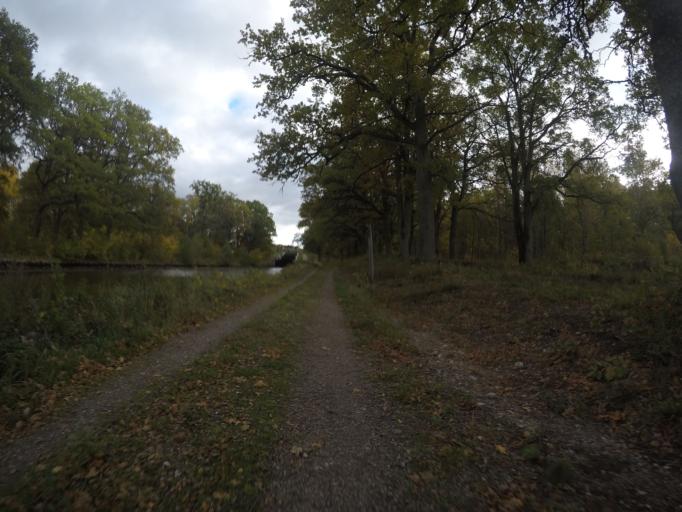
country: SE
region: Vaestmanland
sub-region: Arboga Kommun
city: Tyringe
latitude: 59.3839
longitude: 15.9409
